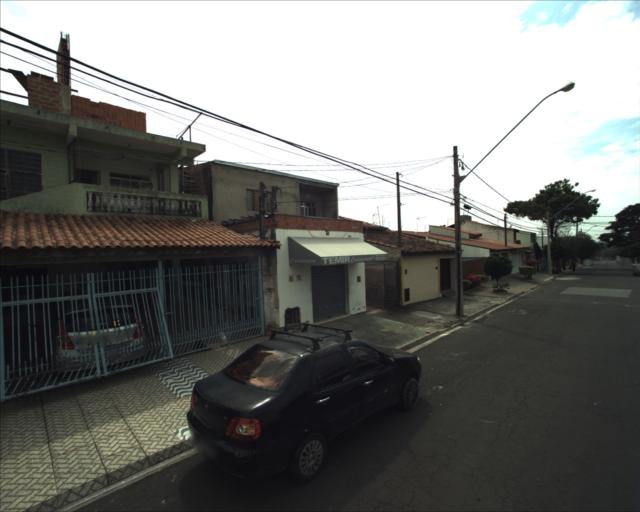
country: BR
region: Sao Paulo
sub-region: Sorocaba
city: Sorocaba
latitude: -23.4990
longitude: -47.5251
